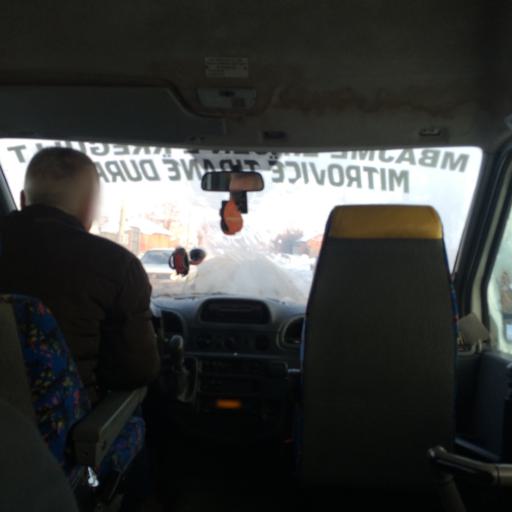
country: XK
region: Pristina
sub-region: Komuna e Drenasit
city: Glogovac
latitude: 42.5924
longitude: 20.8922
